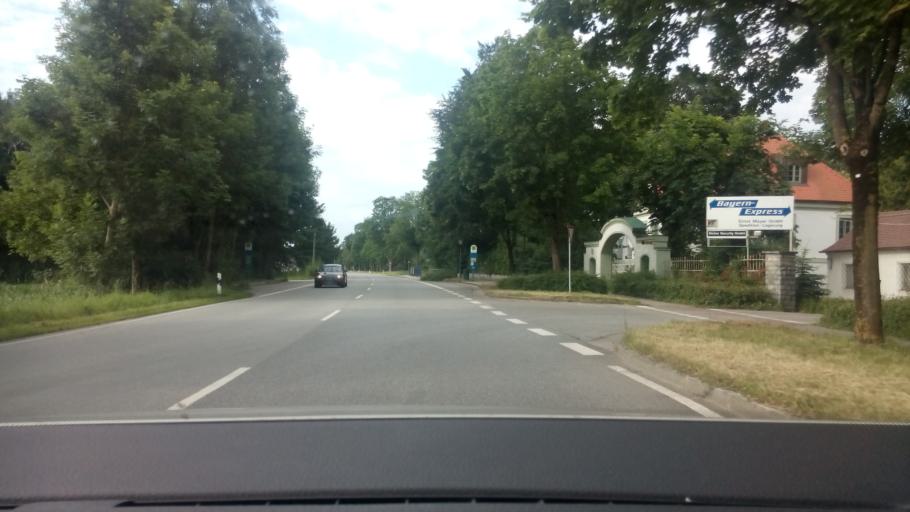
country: DE
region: Bavaria
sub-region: Upper Bavaria
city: Garching bei Munchen
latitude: 48.2379
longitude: 11.6425
